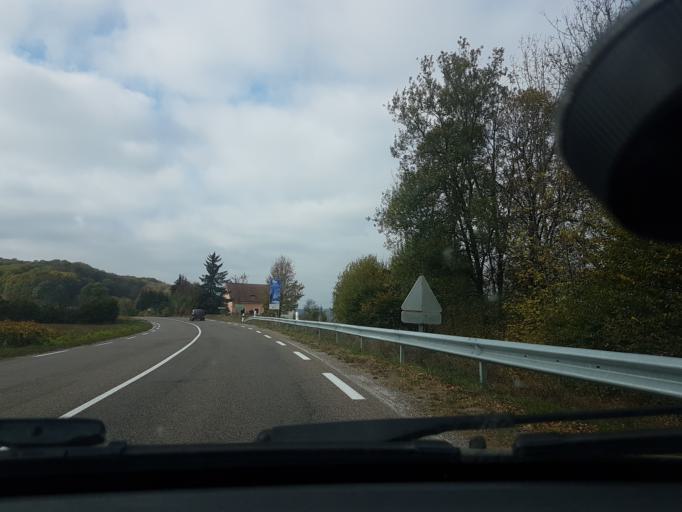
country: FR
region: Franche-Comte
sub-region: Departement de la Haute-Saone
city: Chalonvillars
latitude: 47.6496
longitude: 6.7673
